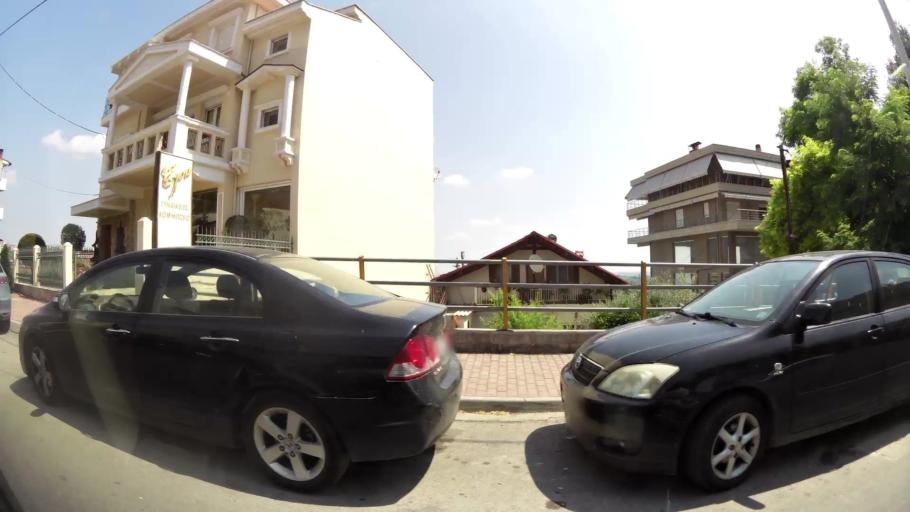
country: GR
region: Central Macedonia
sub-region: Nomos Imathias
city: Veroia
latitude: 40.5142
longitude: 22.2094
